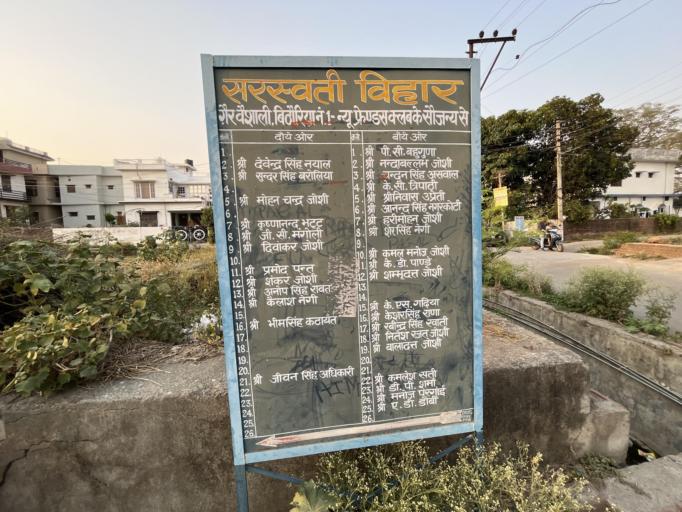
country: IN
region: Uttarakhand
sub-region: Naini Tal
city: Haldwani
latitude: 29.2288
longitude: 79.5099
